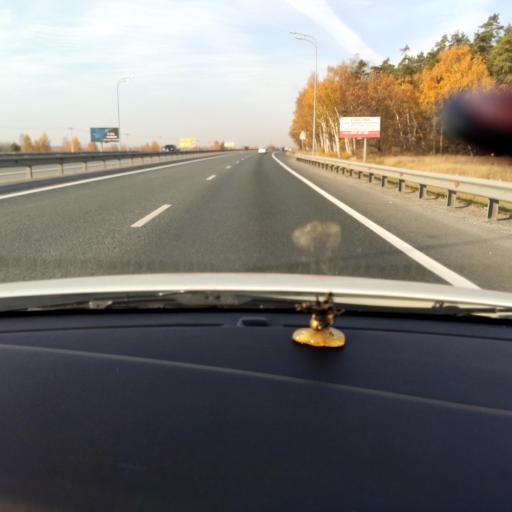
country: RU
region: Tatarstan
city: Osinovo
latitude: 55.9018
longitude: 48.9472
